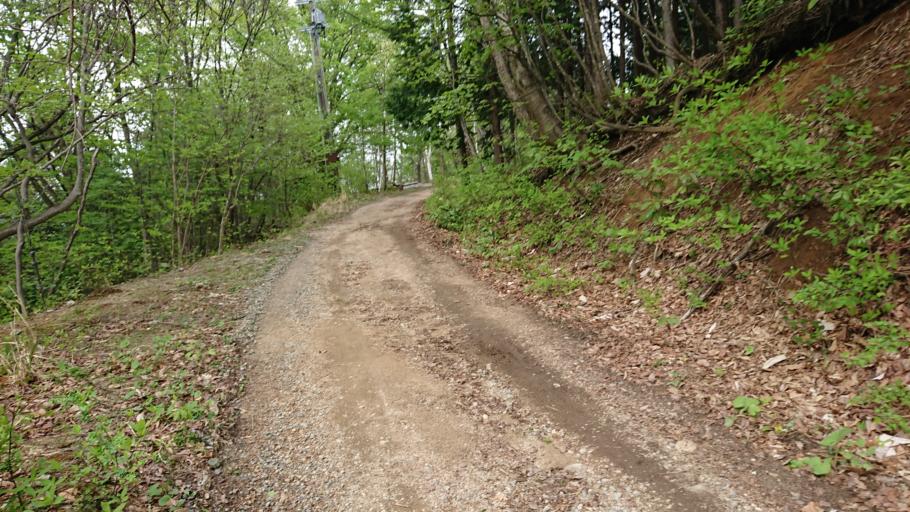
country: JP
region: Nagano
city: Omachi
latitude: 36.5063
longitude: 137.8006
